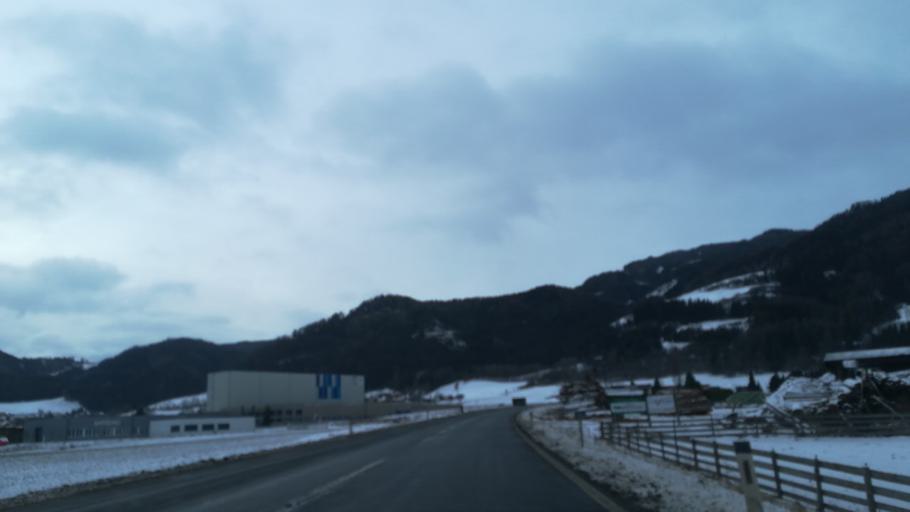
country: AT
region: Styria
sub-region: Politischer Bezirk Murtal
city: Sankt Peter ob Judenburg
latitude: 47.1867
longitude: 14.5999
